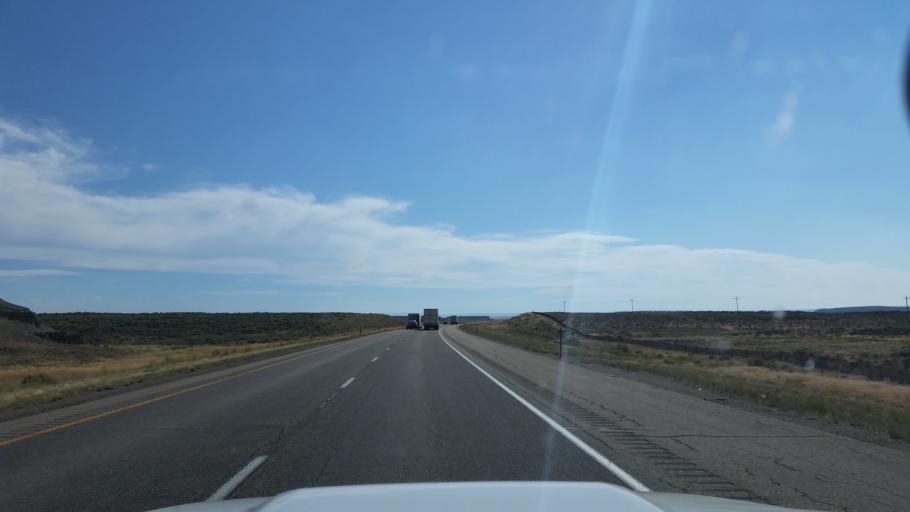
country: US
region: Wyoming
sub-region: Uinta County
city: Lyman
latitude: 41.4129
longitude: -110.1461
